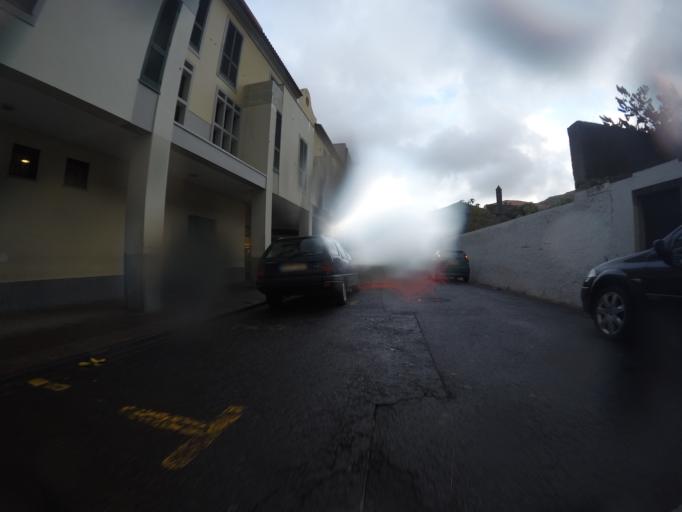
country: PT
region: Madeira
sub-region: Machico
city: Machico
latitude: 32.7200
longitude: -16.7680
